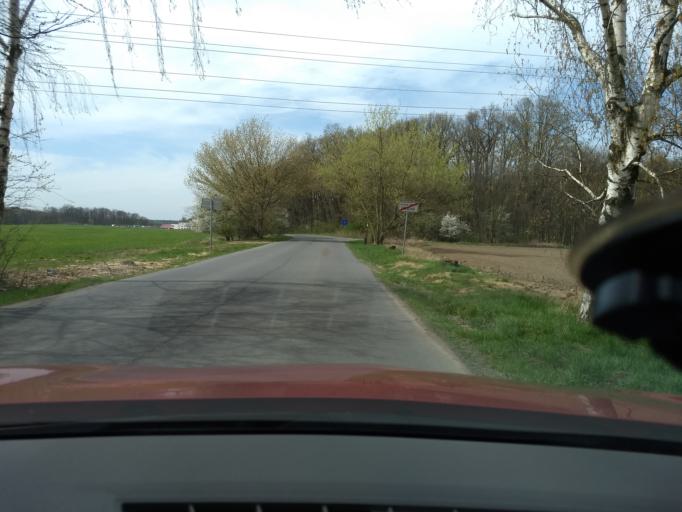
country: CZ
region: Central Bohemia
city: Hostivice
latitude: 50.0675
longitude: 14.2591
